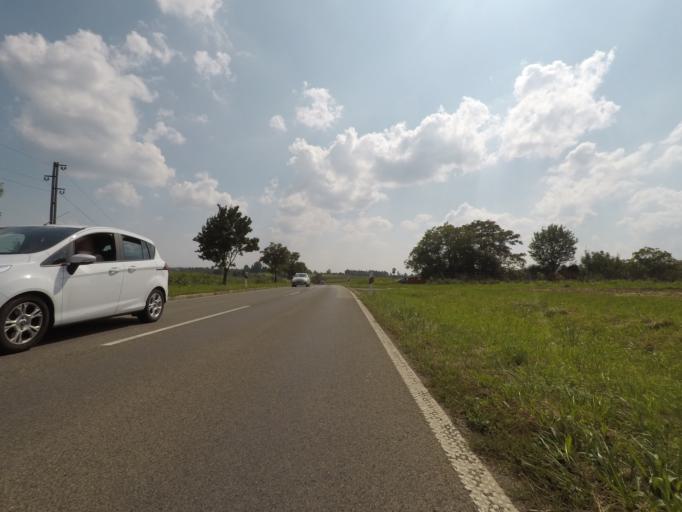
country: DE
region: Baden-Wuerttemberg
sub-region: Regierungsbezirk Stuttgart
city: Weinstadt-Endersbach
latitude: 48.7745
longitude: 9.3893
